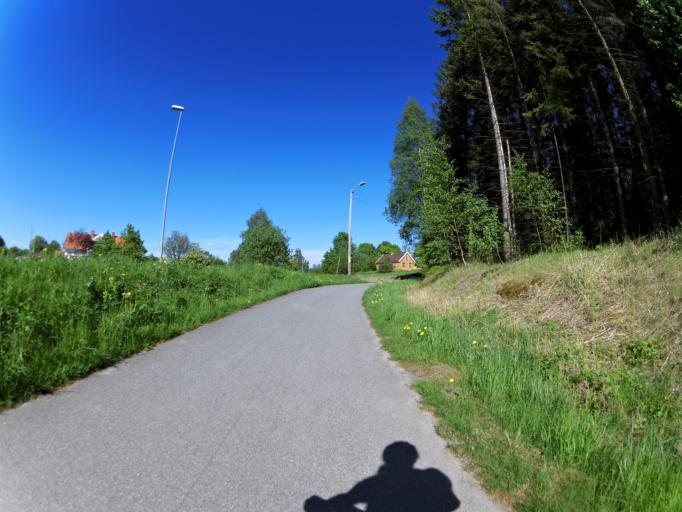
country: NO
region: Ostfold
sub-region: Sarpsborg
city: Sarpsborg
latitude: 59.2243
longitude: 11.0401
